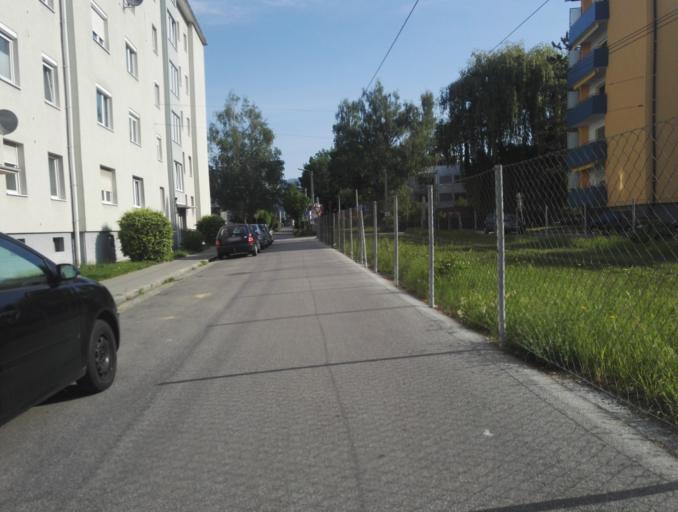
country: AT
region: Styria
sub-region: Graz Stadt
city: Goesting
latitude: 47.1004
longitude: 15.4213
